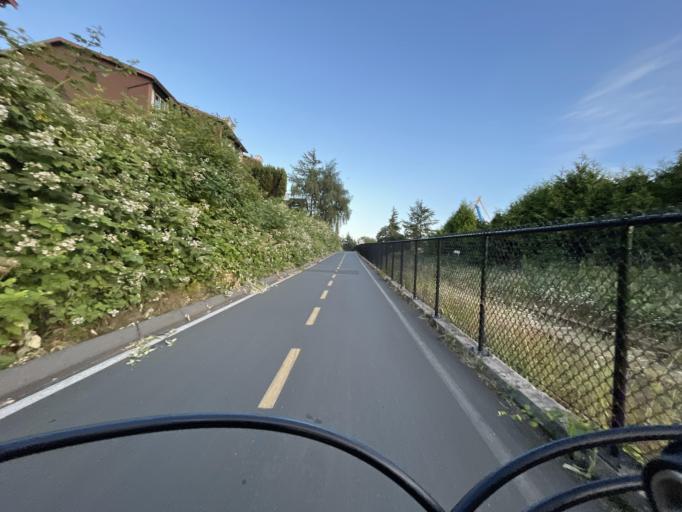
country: CA
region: British Columbia
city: Colwood
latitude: 48.4396
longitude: -123.4289
